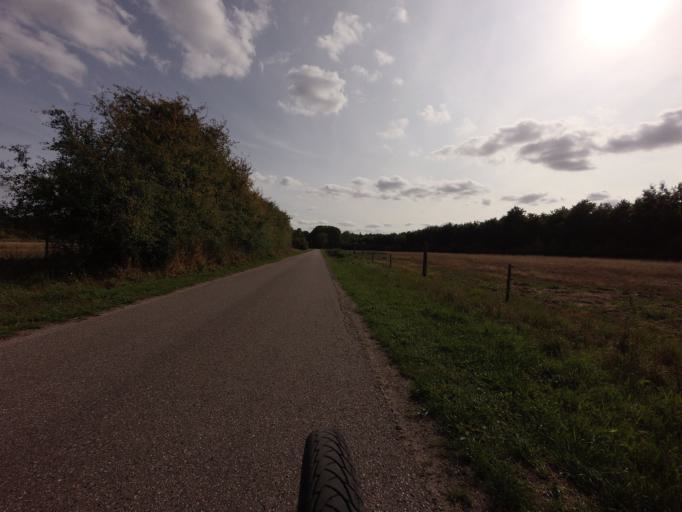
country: DK
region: Zealand
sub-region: Vordingborg Kommune
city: Praesto
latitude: 55.1607
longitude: 12.0924
